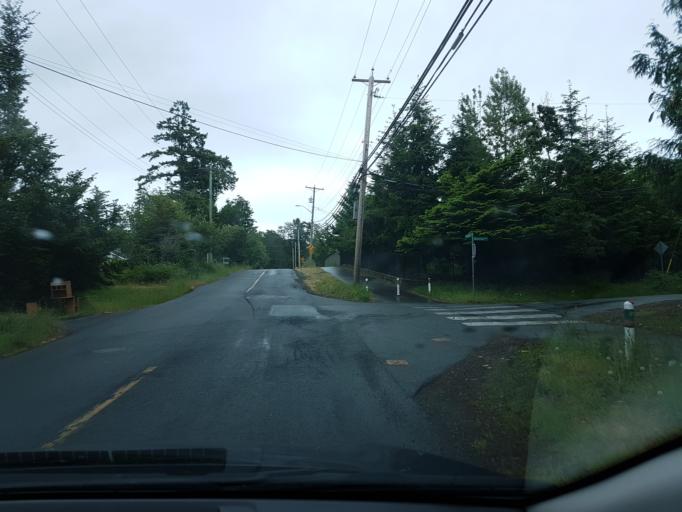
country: CA
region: British Columbia
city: Victoria
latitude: 48.4778
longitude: -123.3474
